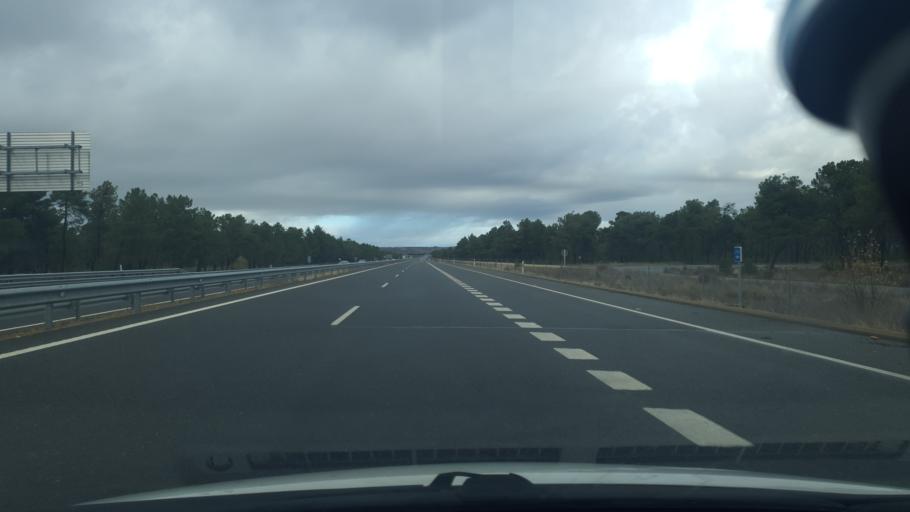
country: ES
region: Castille and Leon
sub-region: Provincia de Segovia
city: Sanchonuno
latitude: 41.3454
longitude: -4.3018
